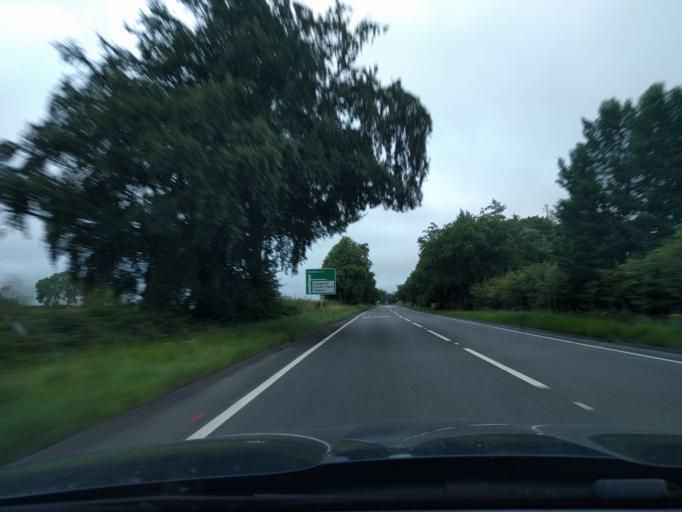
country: GB
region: England
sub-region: Northumberland
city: Hebron
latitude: 55.1990
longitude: -1.7138
